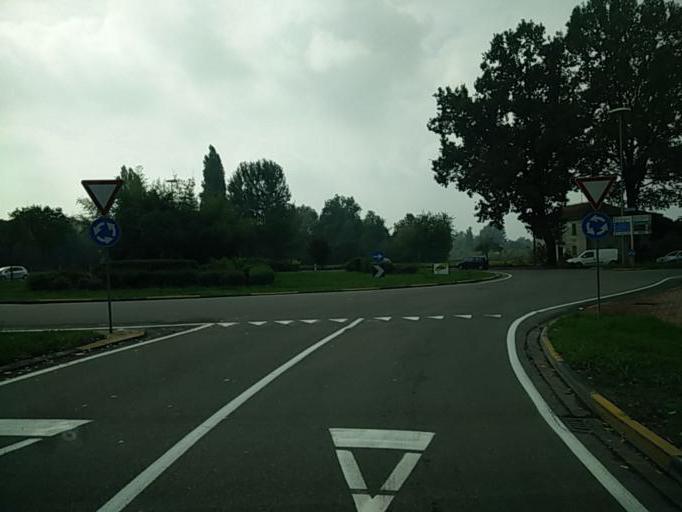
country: IT
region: Emilia-Romagna
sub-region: Provincia di Modena
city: Carpi Centro
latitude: 44.7814
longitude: 10.8671
